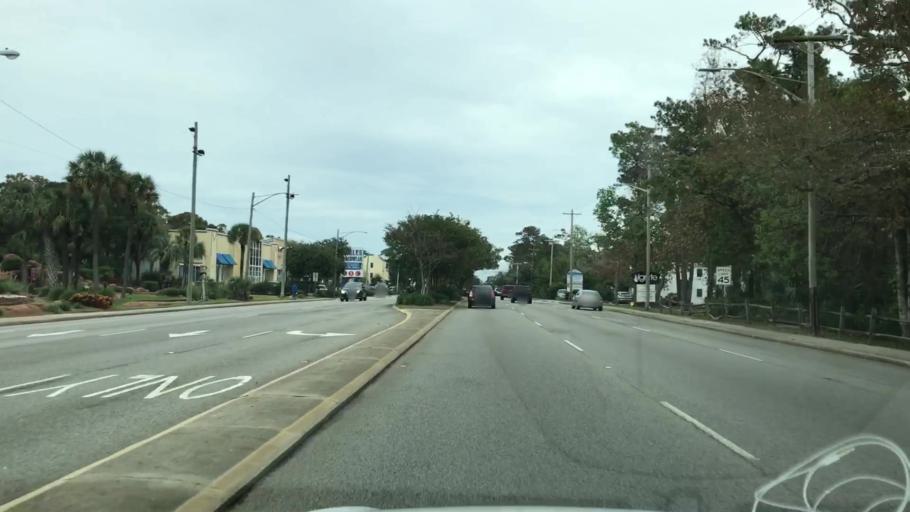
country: US
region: South Carolina
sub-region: Horry County
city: Myrtle Beach
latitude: 33.7229
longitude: -78.8474
